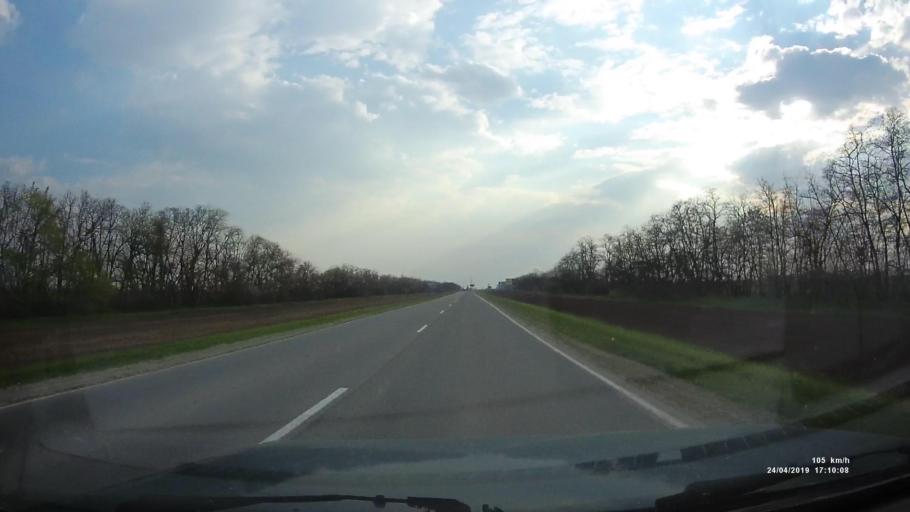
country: RU
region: Rostov
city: Sal'sk
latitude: 46.5049
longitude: 41.5306
